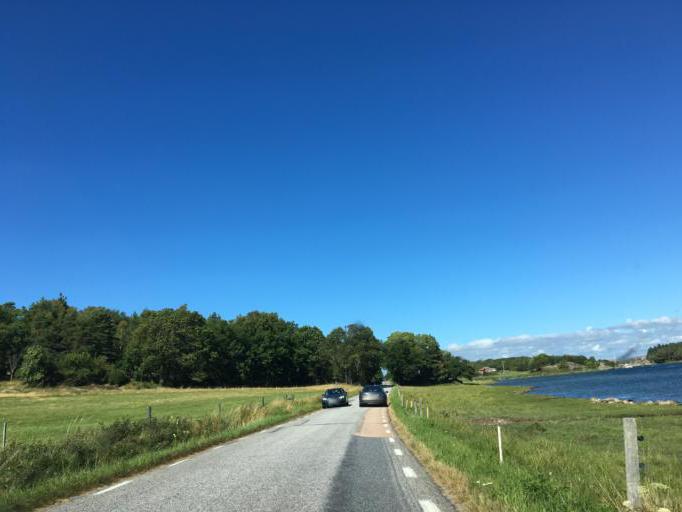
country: SE
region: Vaestra Goetaland
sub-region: Sotenas Kommun
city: Hunnebostrand
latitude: 58.4213
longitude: 11.2653
